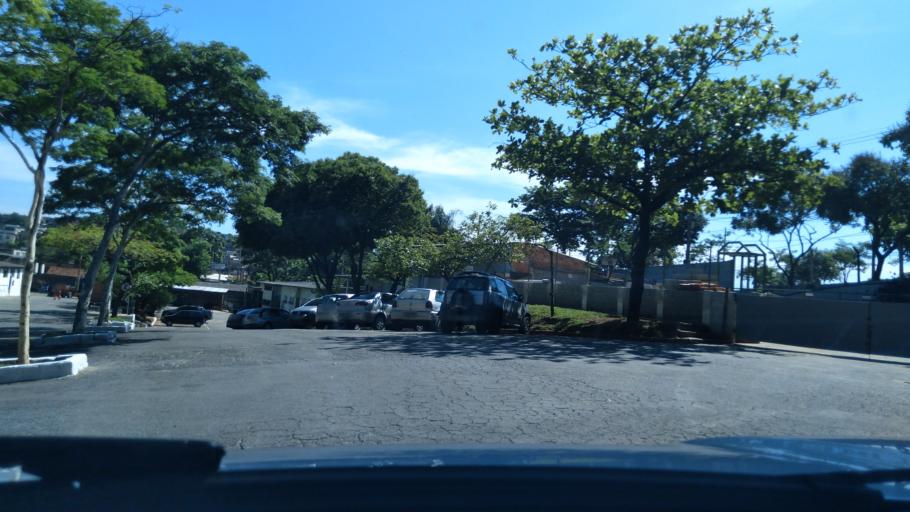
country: BR
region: Minas Gerais
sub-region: Belo Horizonte
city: Belo Horizonte
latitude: -19.8945
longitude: -43.9655
